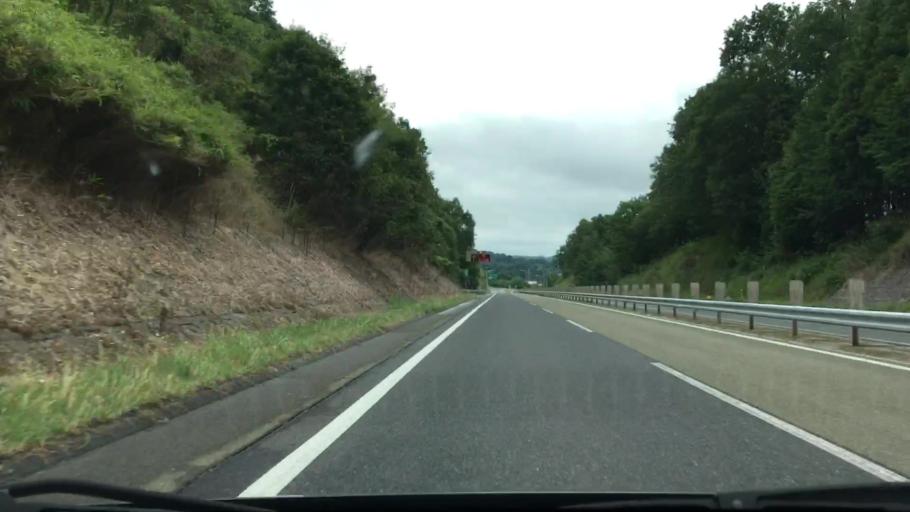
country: JP
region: Hiroshima
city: Shobara
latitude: 34.8443
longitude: 133.0309
